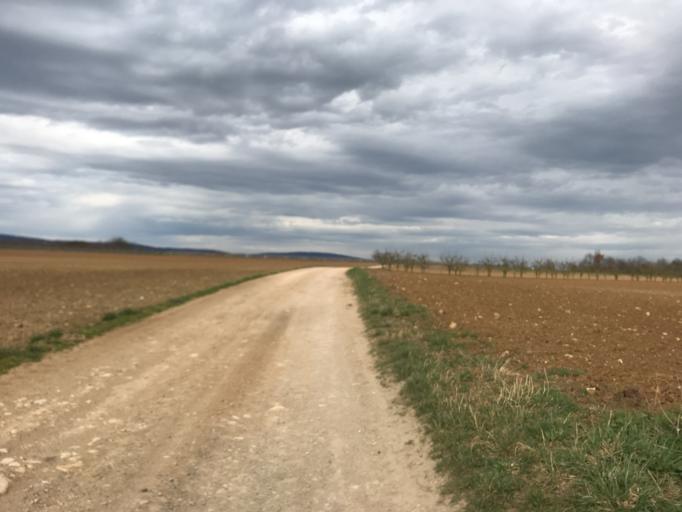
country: DE
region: Rheinland-Pfalz
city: Wackernheim
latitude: 49.9589
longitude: 8.1049
